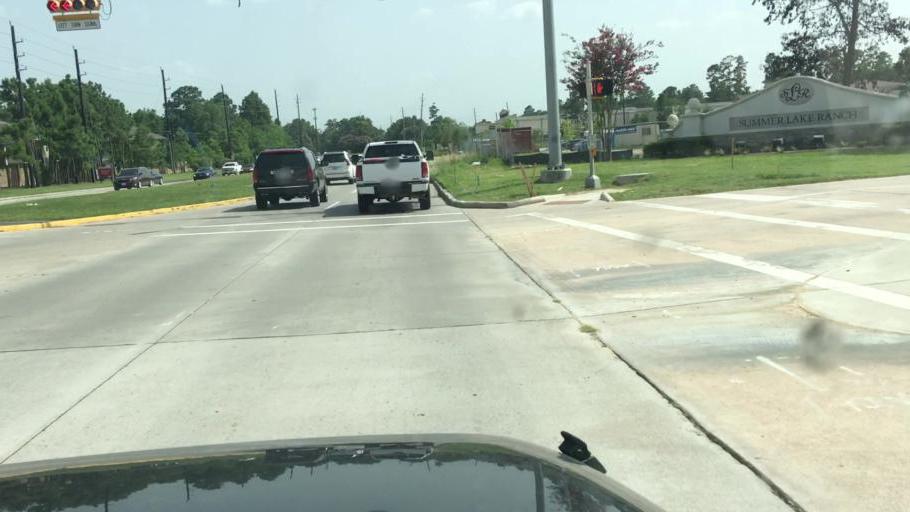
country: US
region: Texas
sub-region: Harris County
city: Atascocita
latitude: 29.9380
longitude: -95.1761
